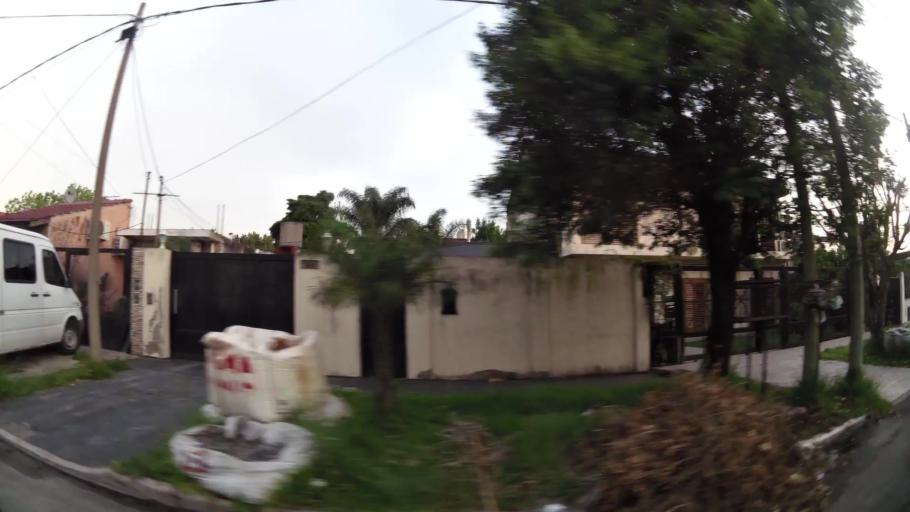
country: AR
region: Buenos Aires
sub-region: Partido de Lomas de Zamora
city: Lomas de Zamora
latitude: -34.7633
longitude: -58.3692
